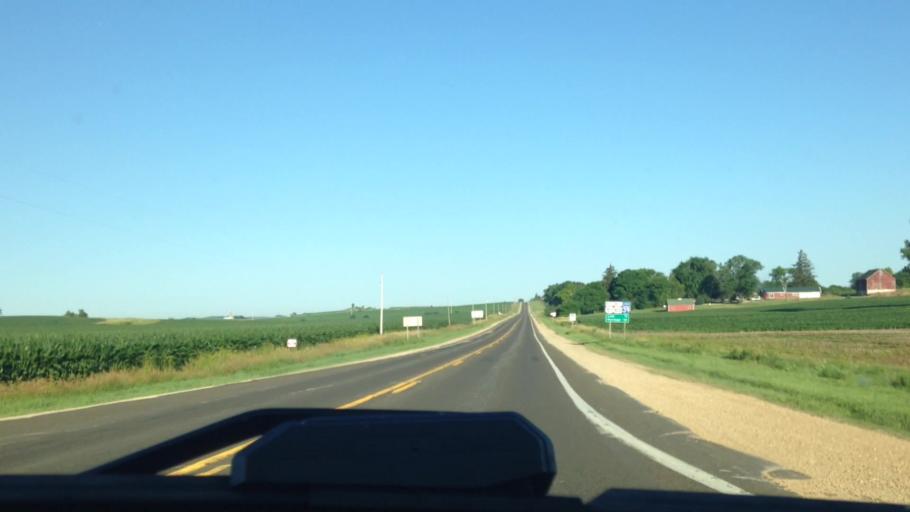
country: US
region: Wisconsin
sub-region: Dane County
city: De Forest
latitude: 43.3322
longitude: -89.3332
